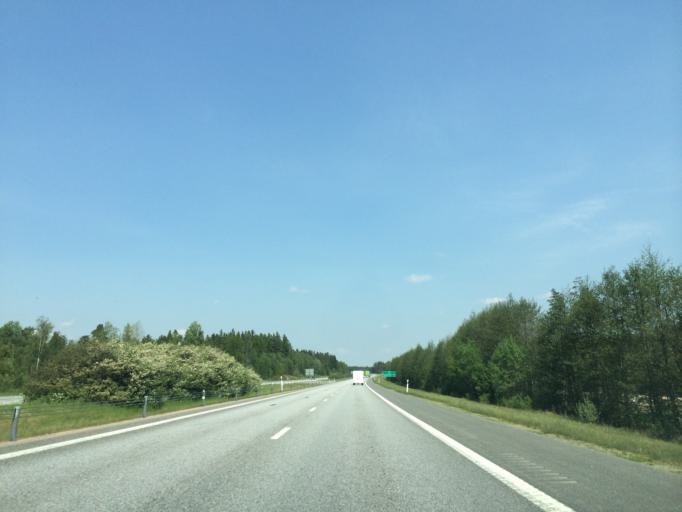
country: SE
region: Joenkoeping
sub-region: Varnamo Kommun
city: Varnamo
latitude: 57.2042
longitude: 14.0822
